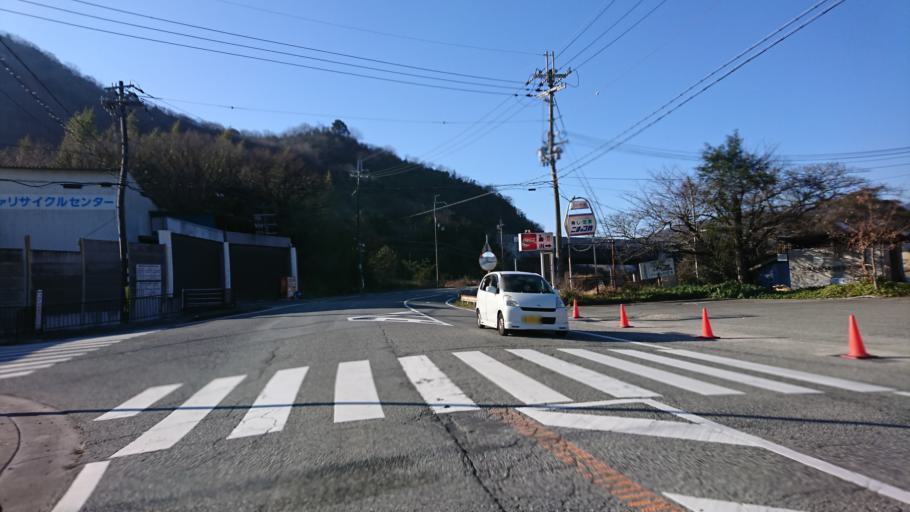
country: JP
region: Hyogo
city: Kakogawacho-honmachi
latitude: 34.8525
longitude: 134.8411
